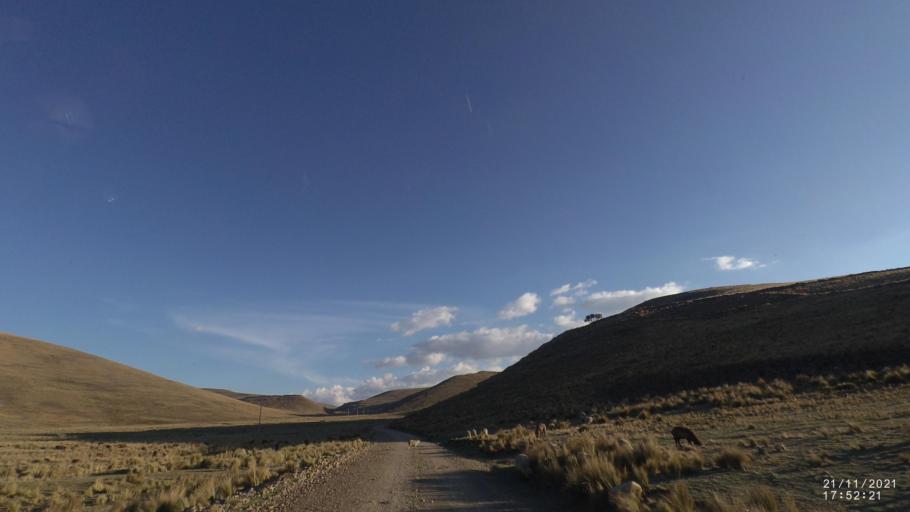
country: BO
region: Cochabamba
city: Cochabamba
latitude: -17.2075
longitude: -66.2418
